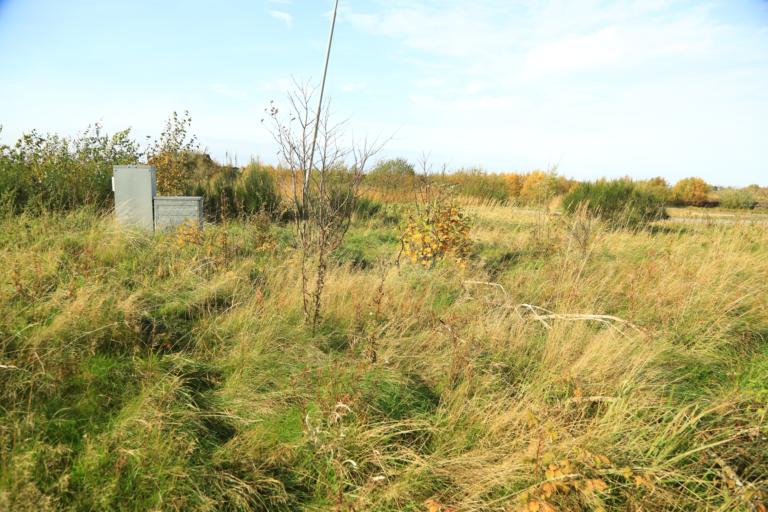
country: SE
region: Halland
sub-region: Varbergs Kommun
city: Varberg
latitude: 57.1206
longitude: 12.2439
